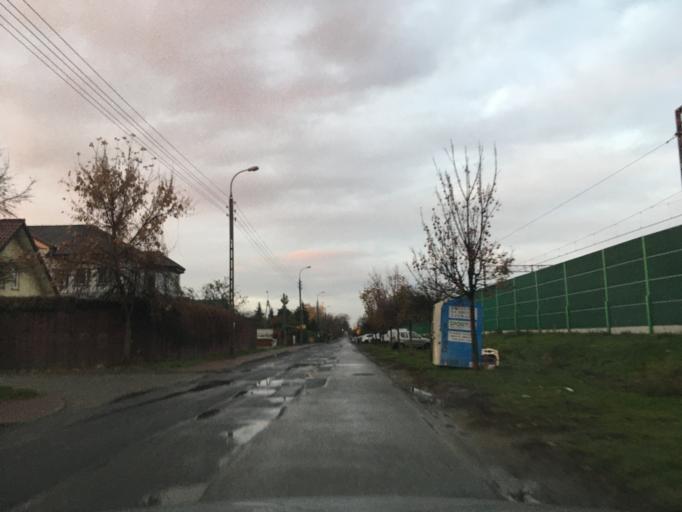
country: PL
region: Masovian Voivodeship
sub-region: Powiat pruszkowski
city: Brwinow
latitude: 52.1430
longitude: 20.7229
